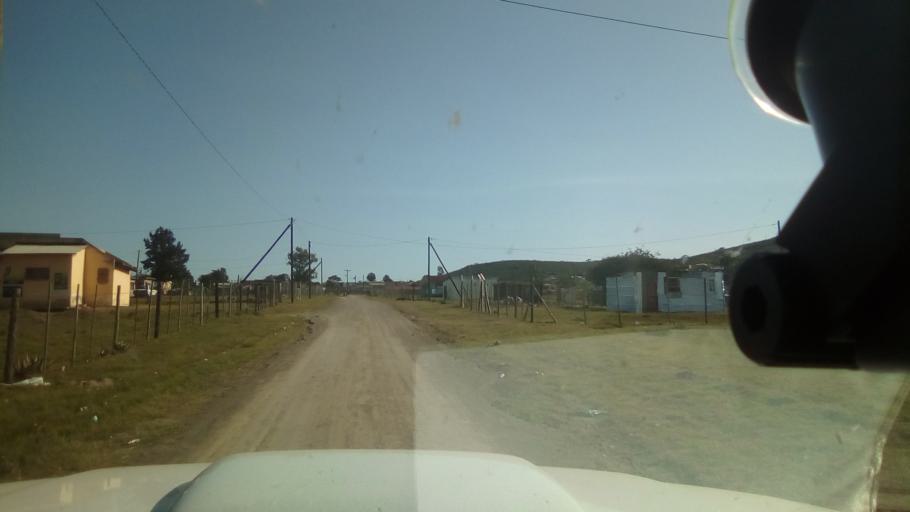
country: ZA
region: Eastern Cape
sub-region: Buffalo City Metropolitan Municipality
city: Bhisho
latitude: -32.8158
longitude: 27.3573
